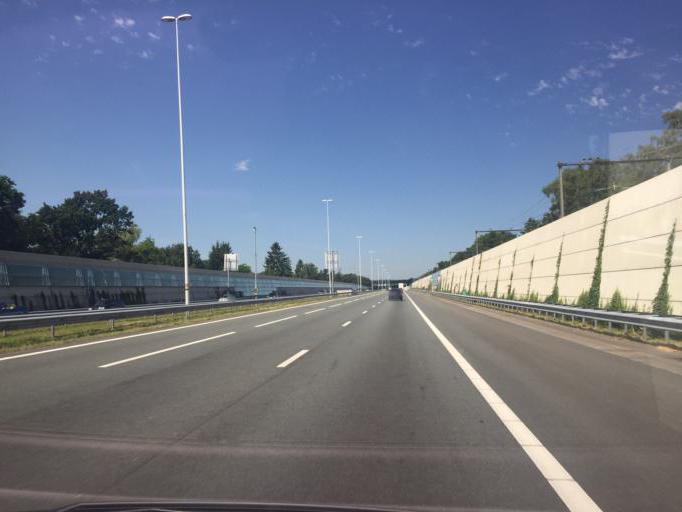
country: NL
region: Utrecht
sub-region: Gemeente Utrechtse Heuvelrug
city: Maarn
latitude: 52.0623
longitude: 5.3776
